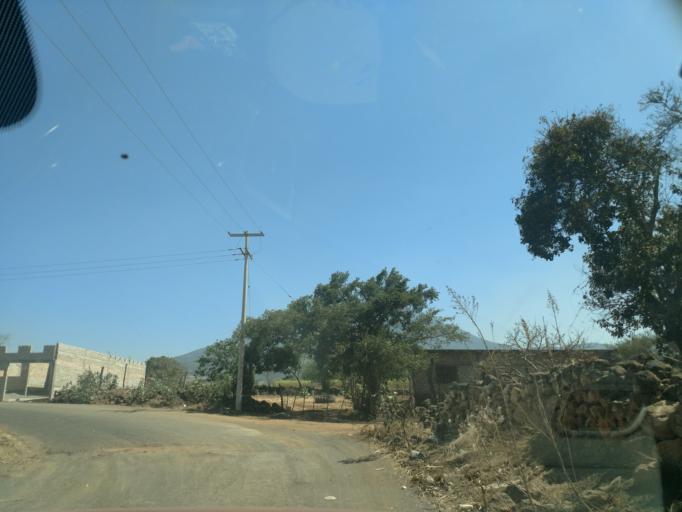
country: MX
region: Nayarit
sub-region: Tepic
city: La Corregidora
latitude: 21.4987
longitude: -104.7030
